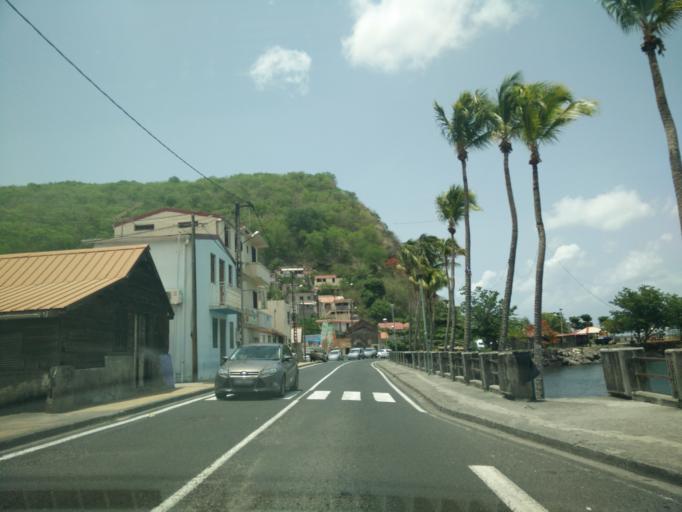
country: MQ
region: Martinique
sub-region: Martinique
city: Saint-Pierre
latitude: 14.6726
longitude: -61.1641
